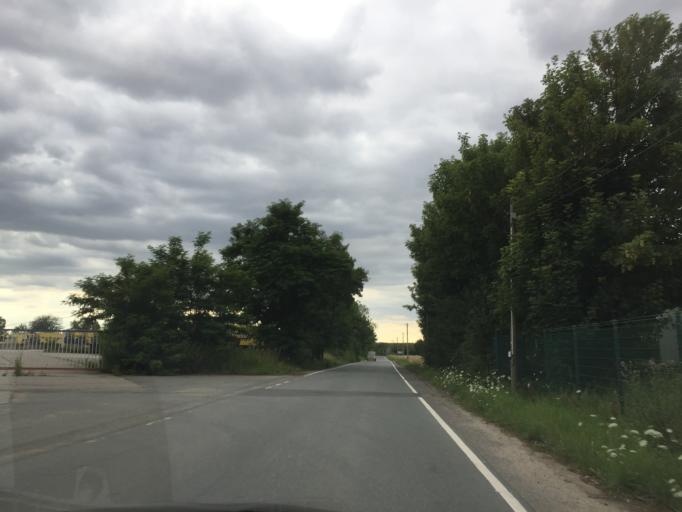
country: DE
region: Thuringia
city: Schmolln
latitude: 50.8752
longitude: 12.3451
